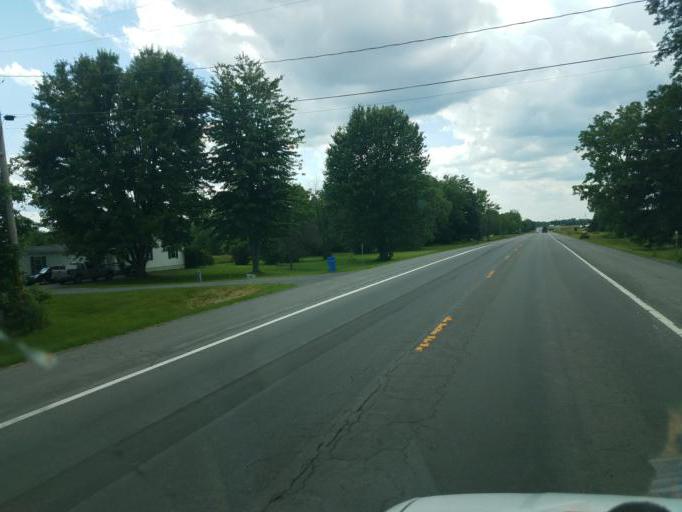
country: US
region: New York
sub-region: Seneca County
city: Waterloo
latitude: 42.9605
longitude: -76.8574
